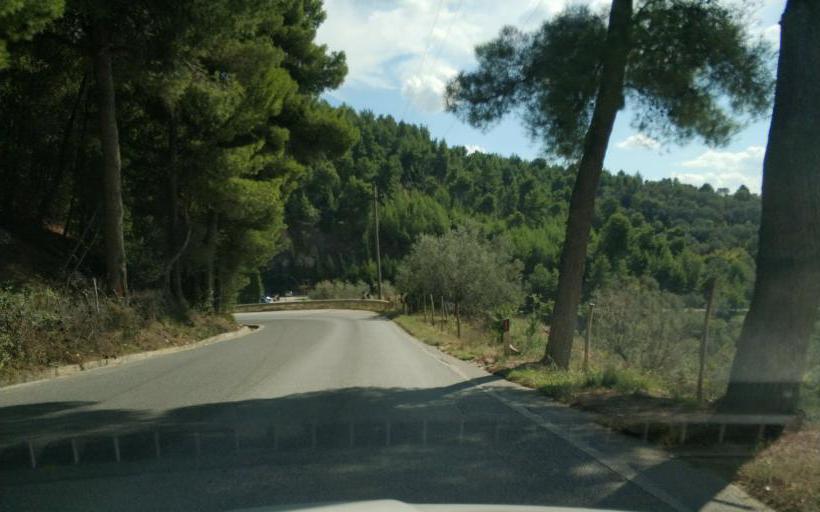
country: AL
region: Durres
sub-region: Rrethi i Krujes
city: Kruje
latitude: 41.4880
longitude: 19.7660
